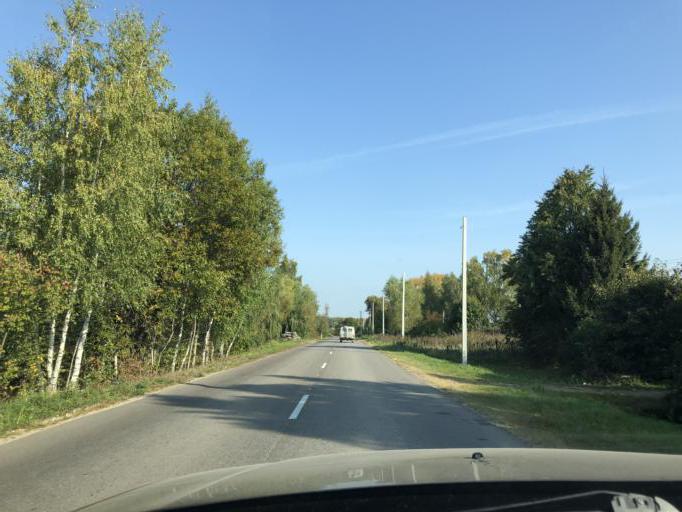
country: RU
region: Tula
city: Novogurovskiy
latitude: 54.4090
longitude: 37.3105
